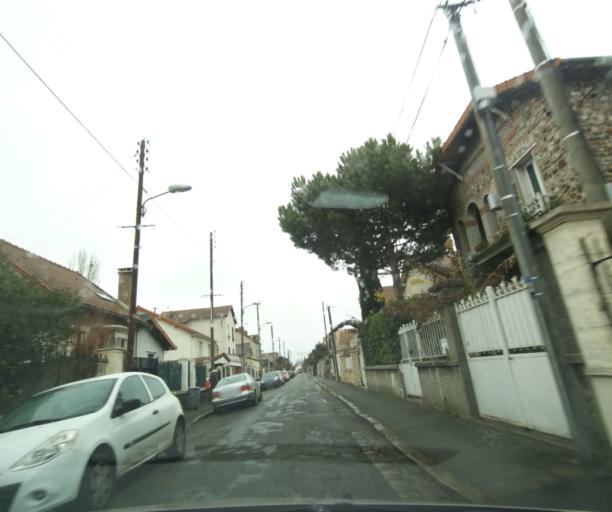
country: FR
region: Ile-de-France
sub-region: Departement du Val-de-Marne
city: Ablon-sur-Seine
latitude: 48.7382
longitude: 2.4215
